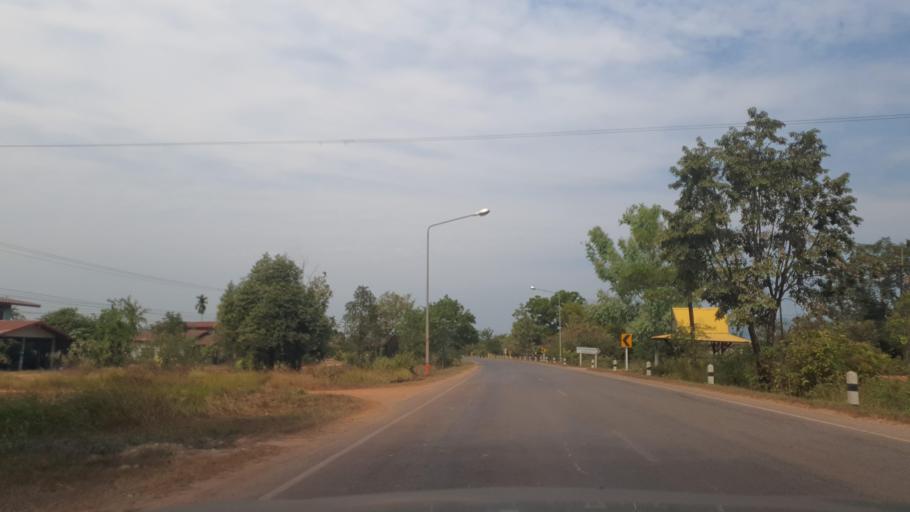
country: TH
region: Changwat Bueng Kan
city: Bung Khla
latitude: 18.2012
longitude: 104.0515
